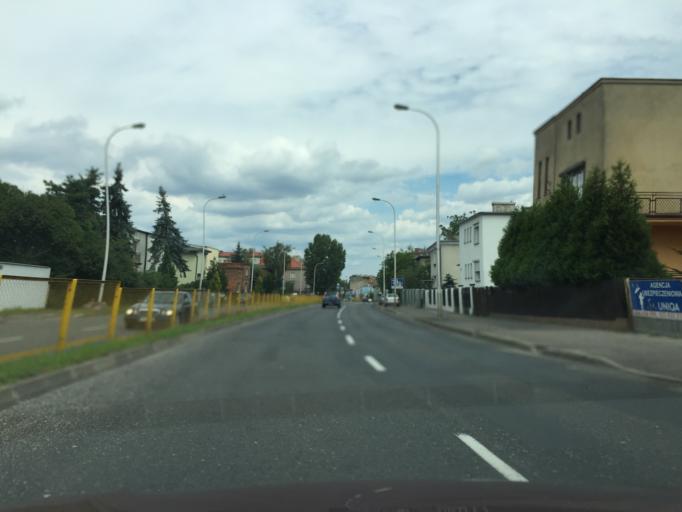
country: PL
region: Greater Poland Voivodeship
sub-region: Kalisz
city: Kalisz
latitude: 51.7557
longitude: 18.0723
